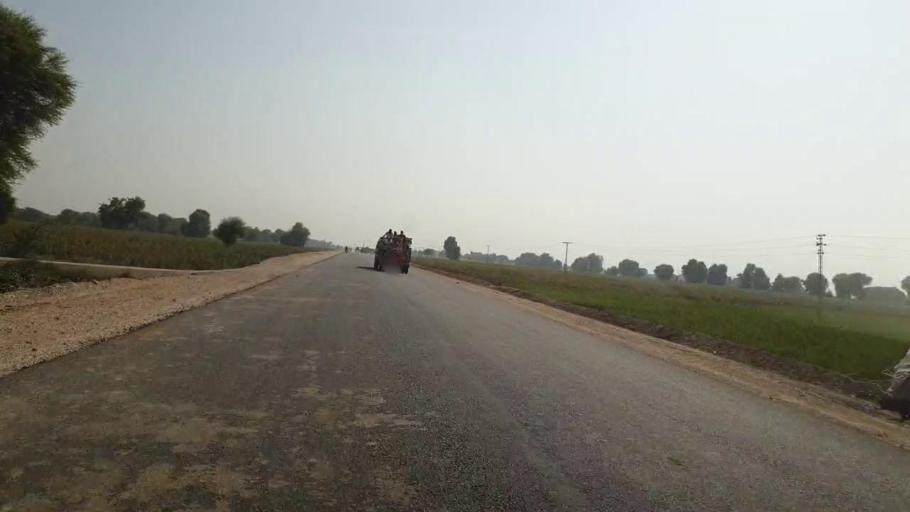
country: PK
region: Sindh
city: Dadu
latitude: 26.6723
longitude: 67.7766
